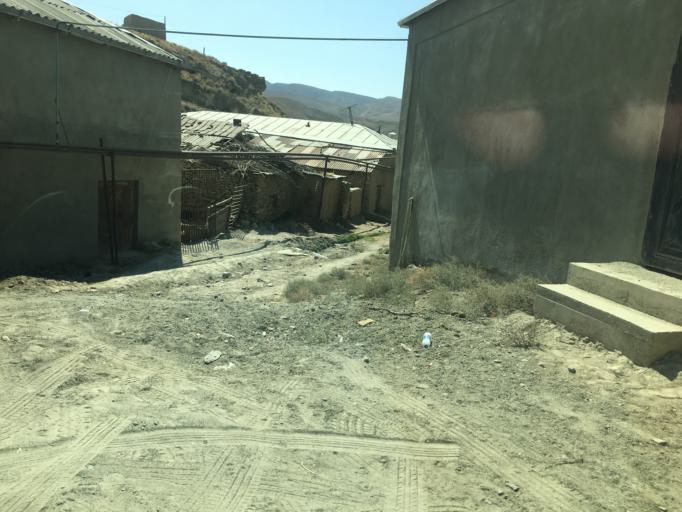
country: TM
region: Ahal
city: Baharly
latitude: 38.3878
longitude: 57.0257
